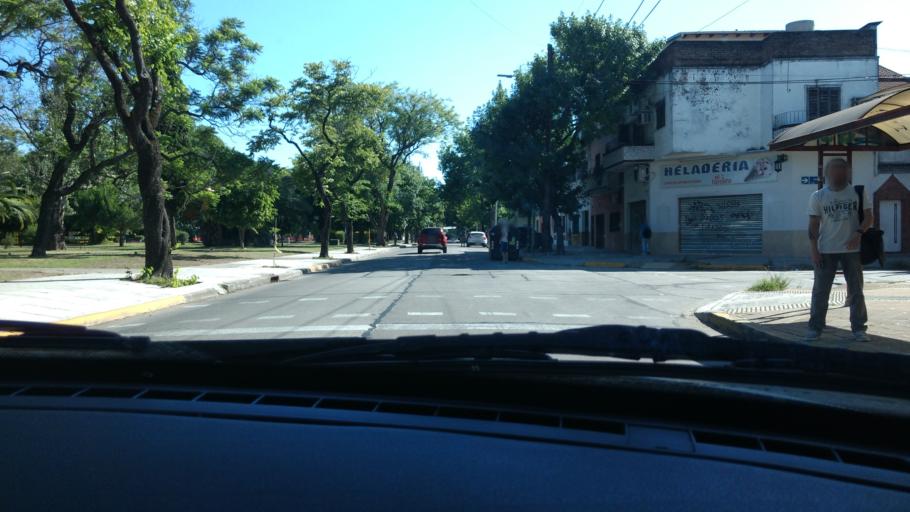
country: AR
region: Buenos Aires F.D.
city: Villa Santa Rita
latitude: -34.6216
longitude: -58.5197
